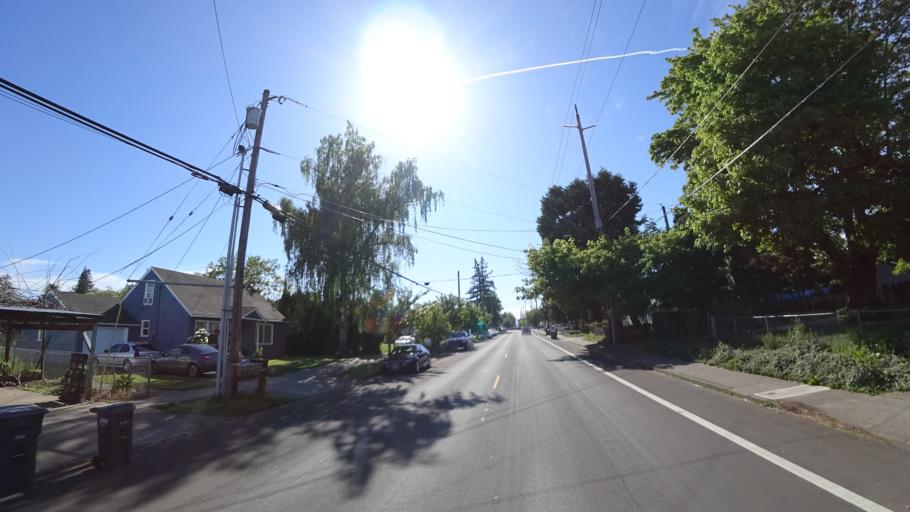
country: US
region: Oregon
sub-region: Washington County
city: Hillsboro
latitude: 45.5200
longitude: -122.9710
